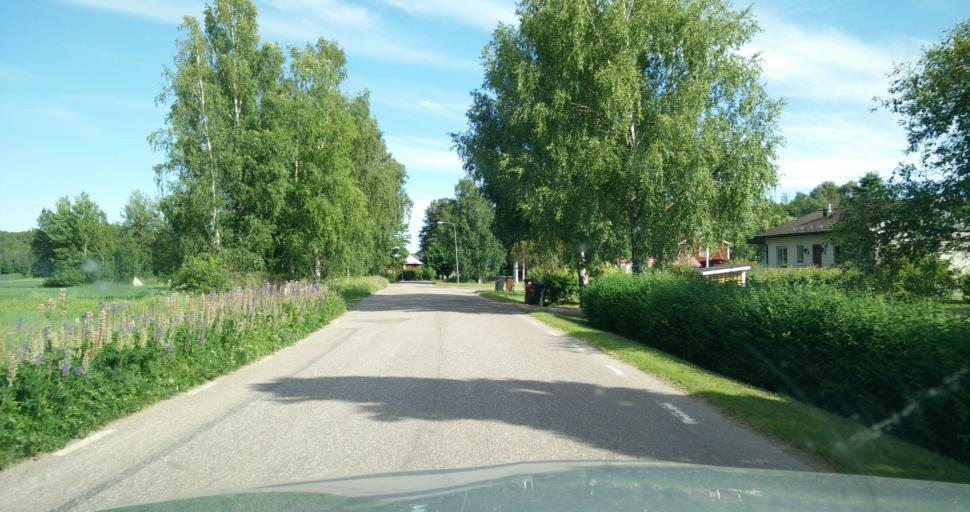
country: SE
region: Dalarna
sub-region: Hedemora Kommun
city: Langshyttan
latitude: 60.3914
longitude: 15.9651
